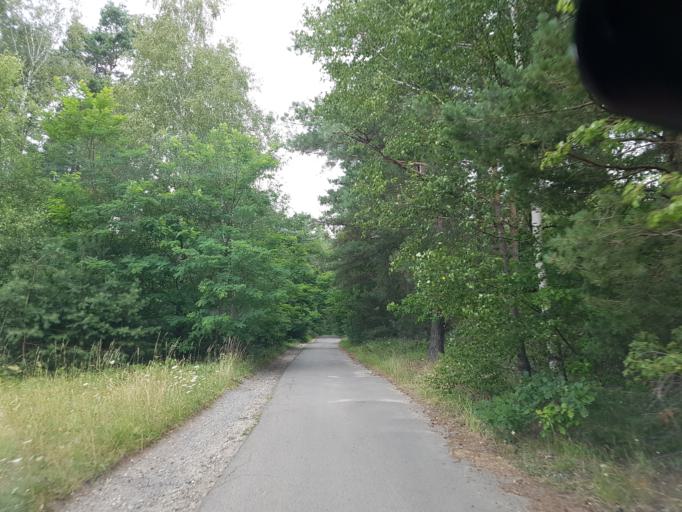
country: DE
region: Brandenburg
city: Sallgast
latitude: 51.5760
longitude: 13.8624
